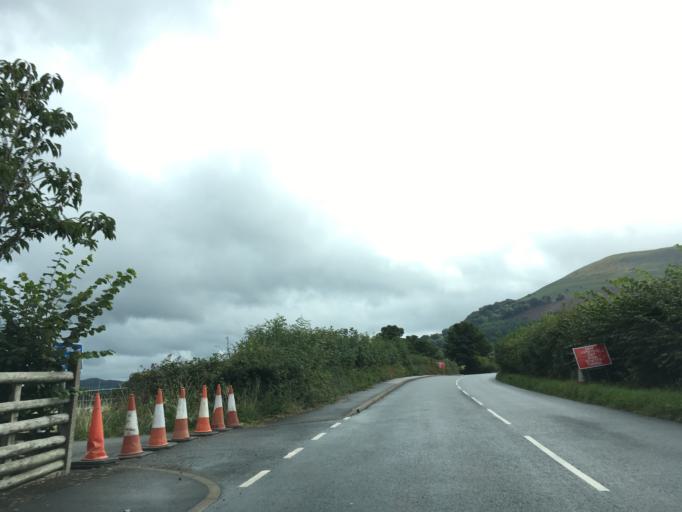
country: GB
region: Wales
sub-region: Monmouthshire
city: Gilwern
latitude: 51.8217
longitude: -3.0732
